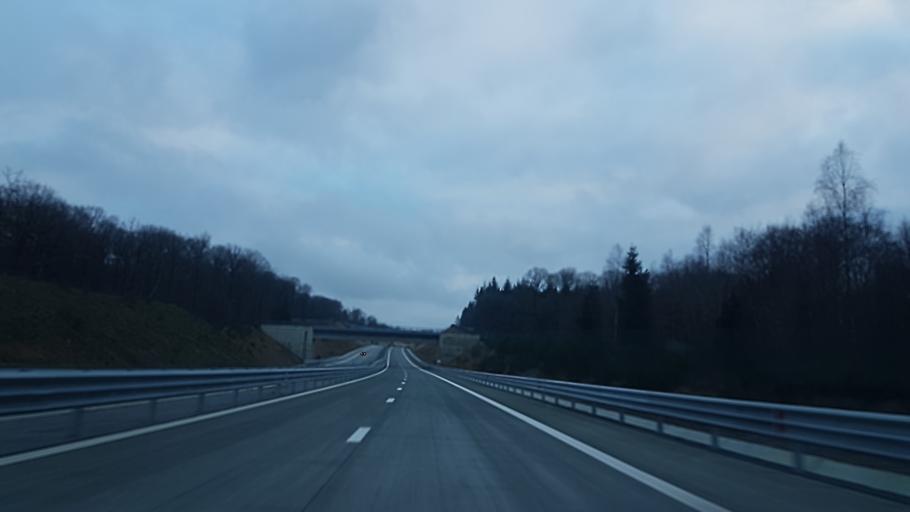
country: BE
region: Wallonia
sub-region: Province de Namur
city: Couvin
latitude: 50.0062
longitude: 4.5382
